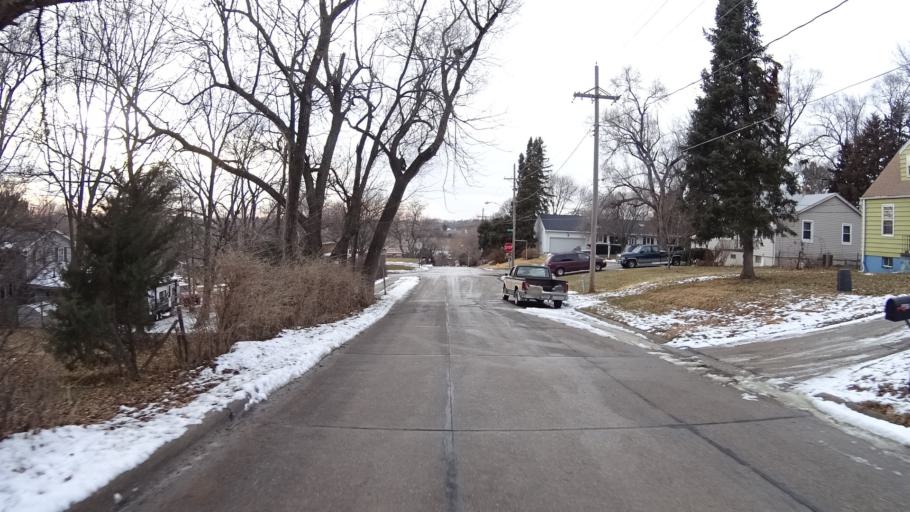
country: US
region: Nebraska
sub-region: Sarpy County
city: Bellevue
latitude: 41.1726
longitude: -95.9203
